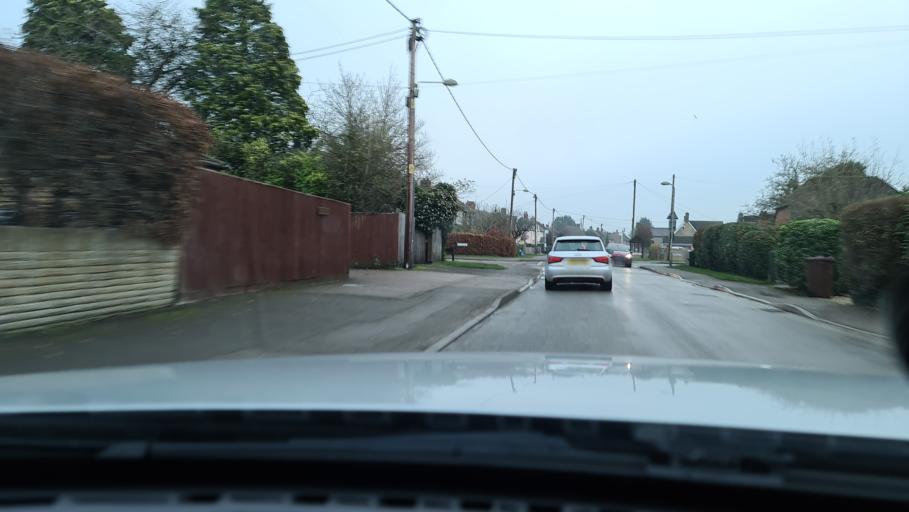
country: GB
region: England
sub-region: Oxfordshire
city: Bicester
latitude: 51.9000
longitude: -1.1205
